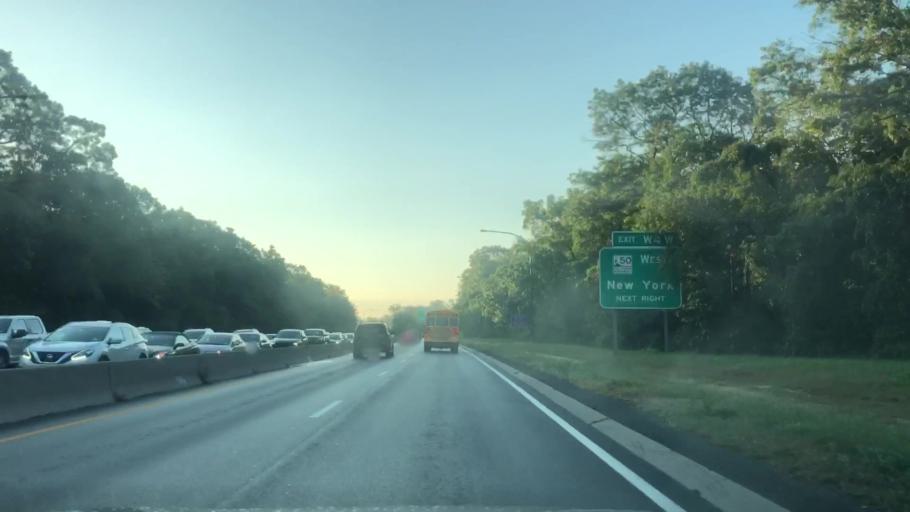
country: US
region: New York
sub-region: Nassau County
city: North Bellmore
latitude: 40.7040
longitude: -73.5234
